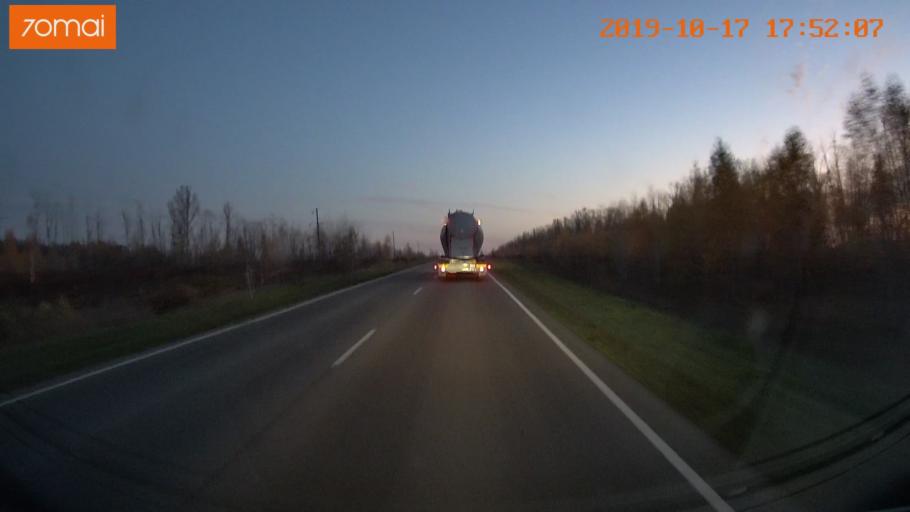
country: RU
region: Tula
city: Kurkino
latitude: 53.6396
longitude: 38.6835
